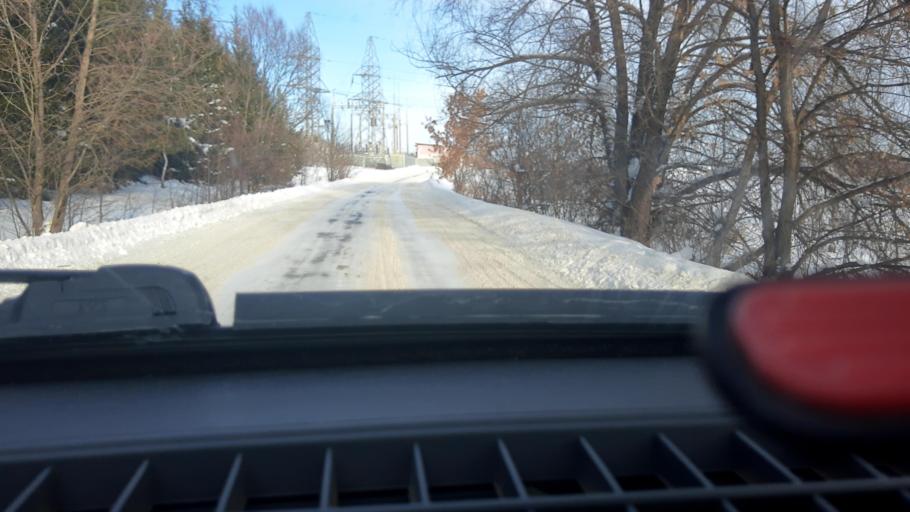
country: RU
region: Bashkortostan
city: Ufa
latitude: 54.5296
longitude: 55.9117
